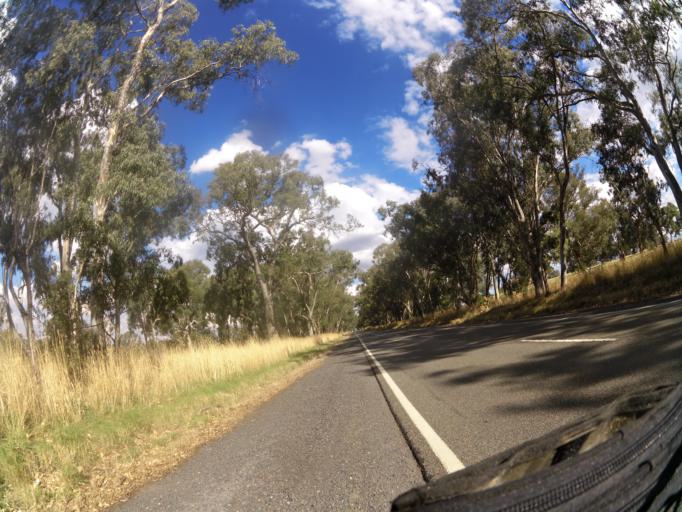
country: AU
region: Victoria
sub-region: Mansfield
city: Mansfield
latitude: -37.0085
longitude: 146.0826
